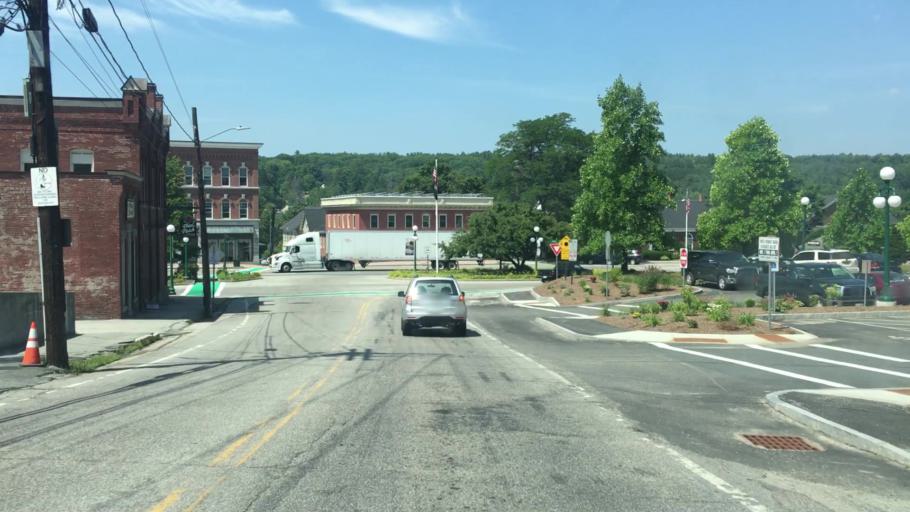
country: US
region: New Hampshire
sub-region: Sullivan County
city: Newport
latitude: 43.3652
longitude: -72.1726
